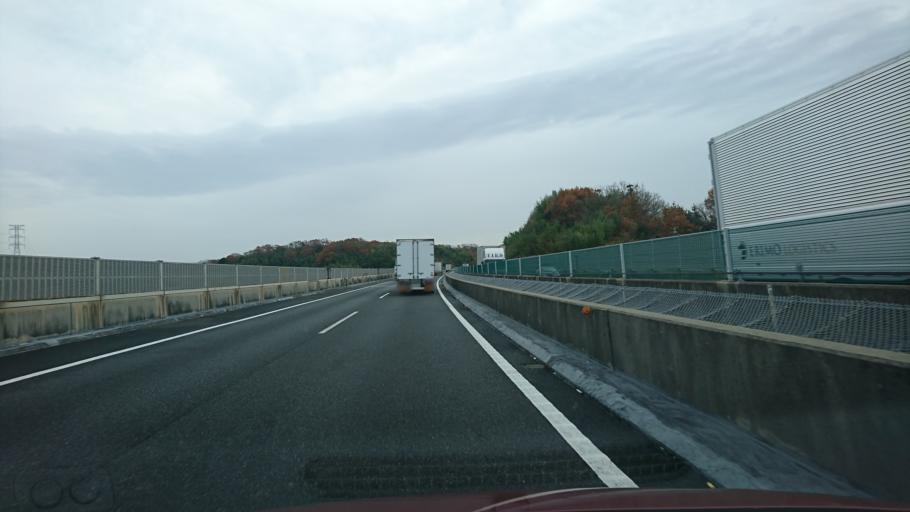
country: JP
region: Hyogo
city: Sandacho
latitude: 34.8314
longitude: 135.1637
